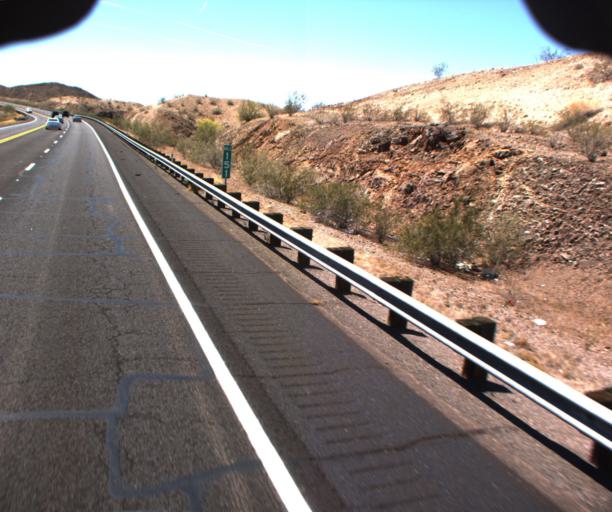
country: US
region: Arizona
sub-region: La Paz County
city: Cienega Springs
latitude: 34.2117
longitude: -114.2016
